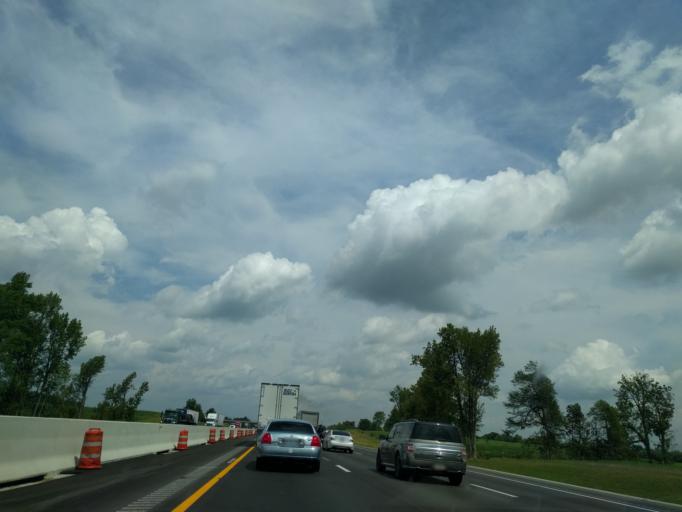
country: US
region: Kentucky
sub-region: Larue County
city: Hodgenville
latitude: 37.5345
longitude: -85.8820
